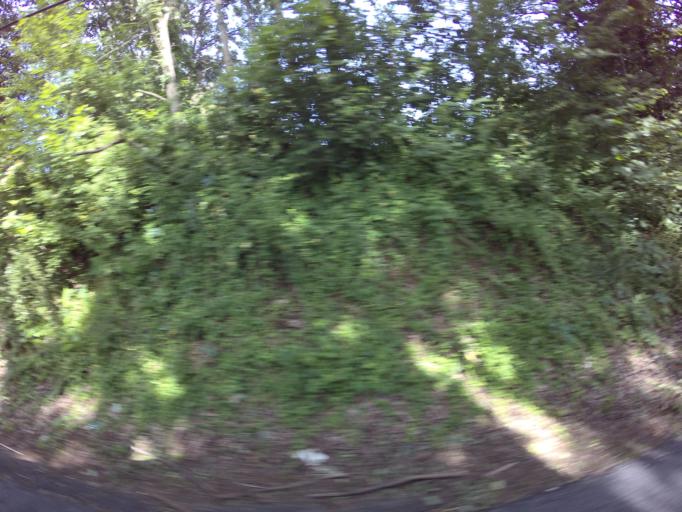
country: US
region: Maryland
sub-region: Frederick County
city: Green Valley
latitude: 39.3688
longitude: -77.2754
